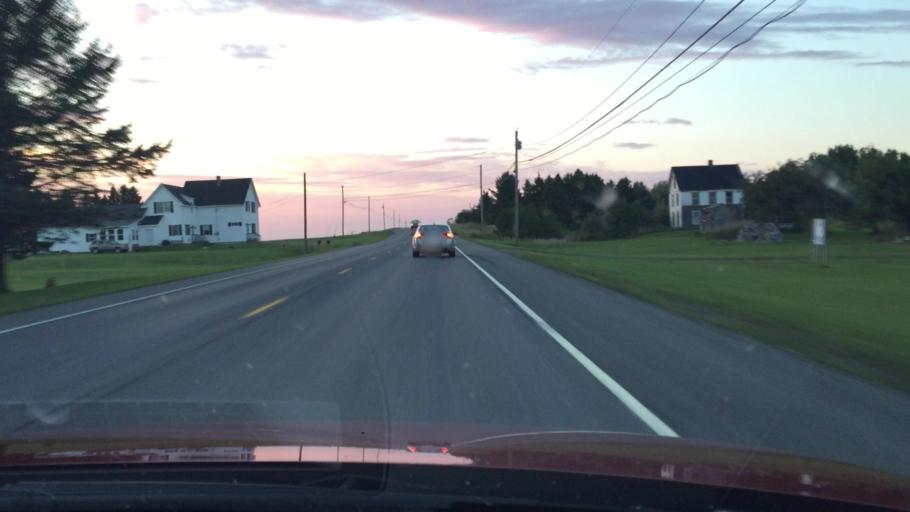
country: US
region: Maine
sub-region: Aroostook County
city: Easton
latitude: 46.5732
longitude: -67.9527
